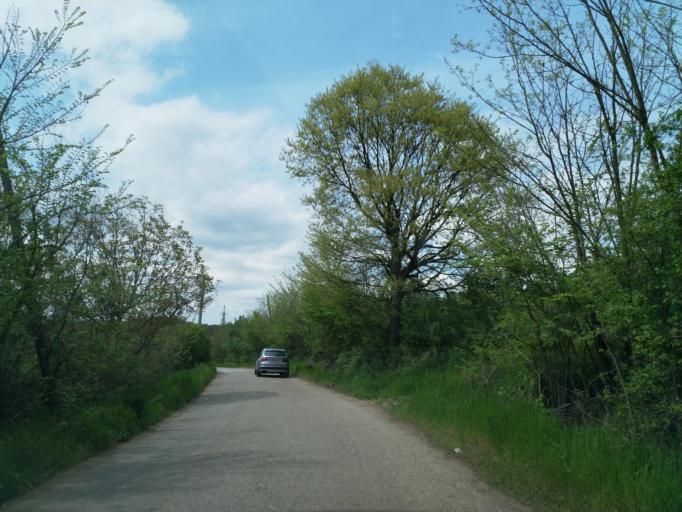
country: RS
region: Central Serbia
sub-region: Pomoravski Okrug
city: Cuprija
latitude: 43.9558
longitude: 21.4791
